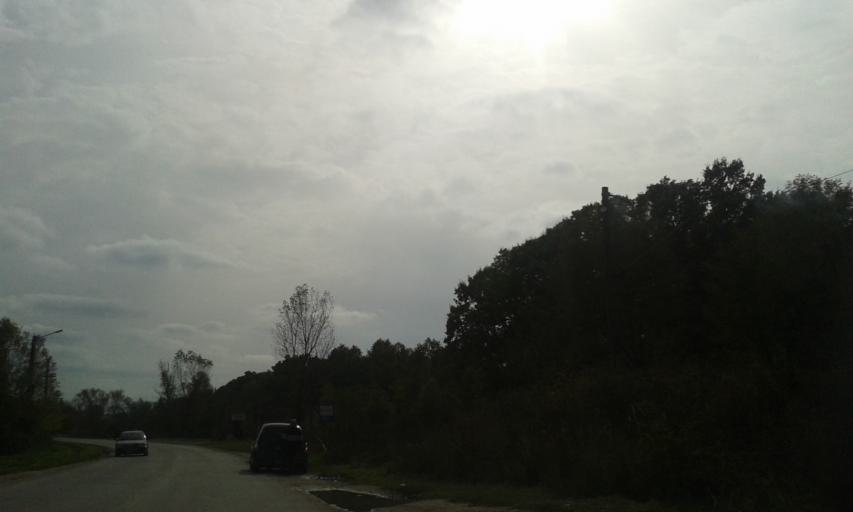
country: RO
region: Gorj
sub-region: Comuna Targu Carbunesti
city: Targu Carbunesti
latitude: 44.9685
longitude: 23.5034
